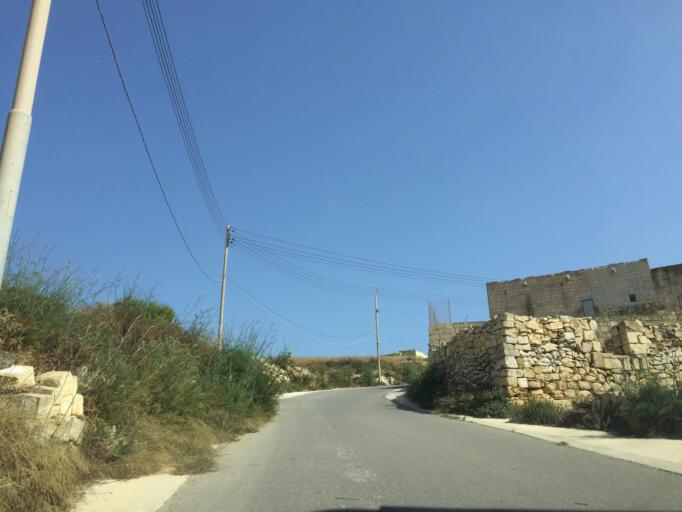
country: MT
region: L-Gharb
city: Gharb
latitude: 36.0659
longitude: 14.2059
